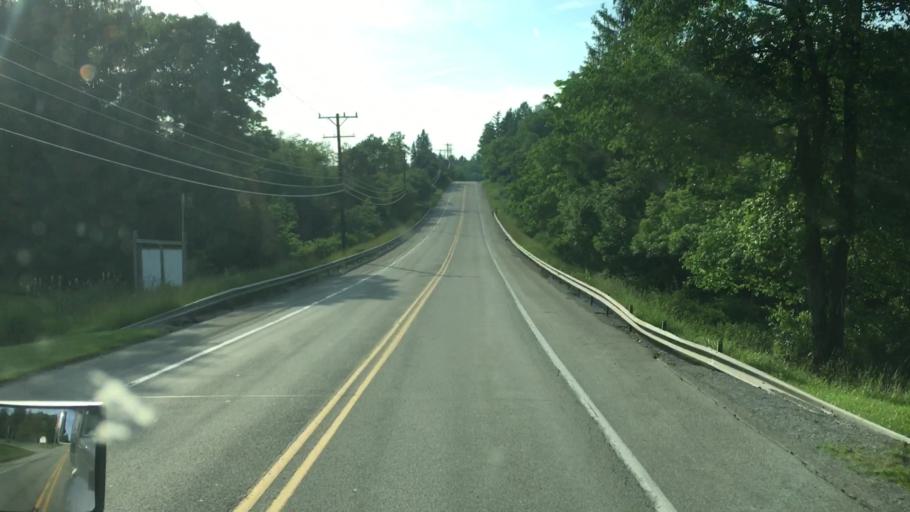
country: US
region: Pennsylvania
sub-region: Fayette County
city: Hopwood
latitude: 39.7999
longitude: -79.5498
